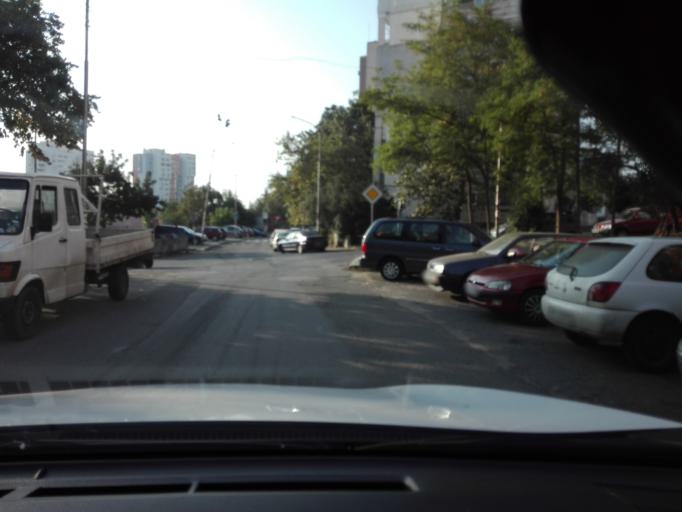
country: BG
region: Burgas
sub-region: Obshtina Burgas
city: Burgas
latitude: 42.4648
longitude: 27.4162
